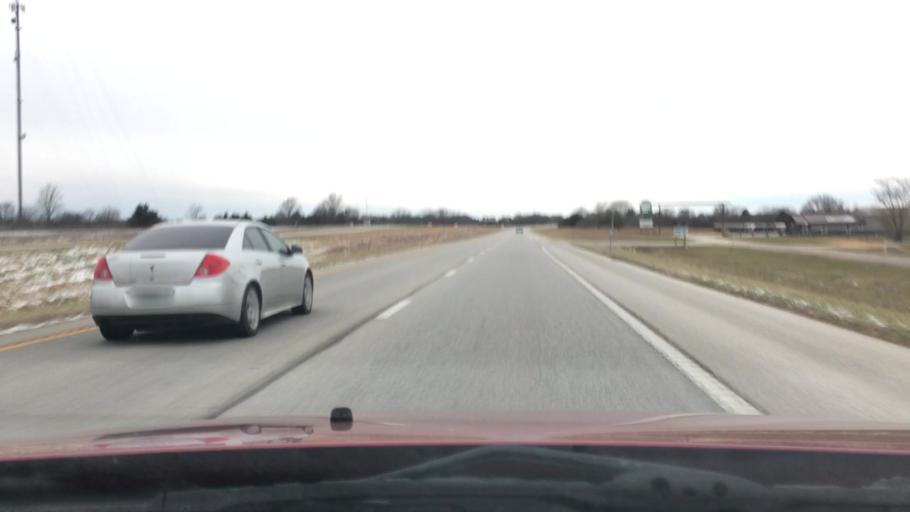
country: US
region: Missouri
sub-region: Webster County
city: Seymour
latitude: 37.1693
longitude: -92.8186
